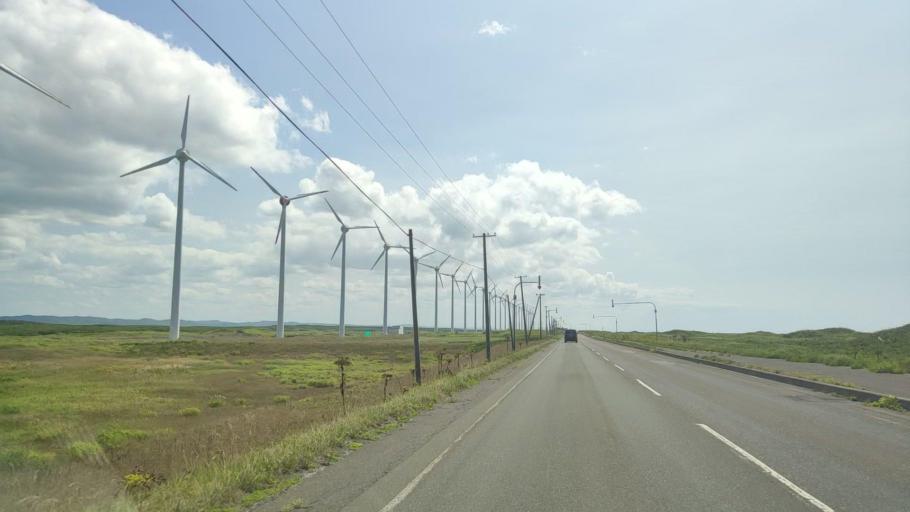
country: JP
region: Hokkaido
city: Makubetsu
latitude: 44.9812
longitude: 141.6931
